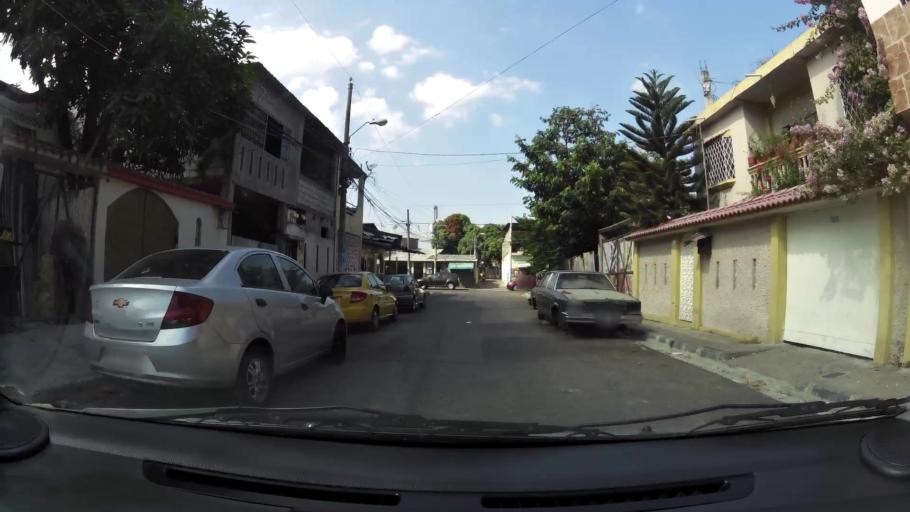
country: EC
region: Guayas
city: Guayaquil
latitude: -2.1586
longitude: -79.9374
